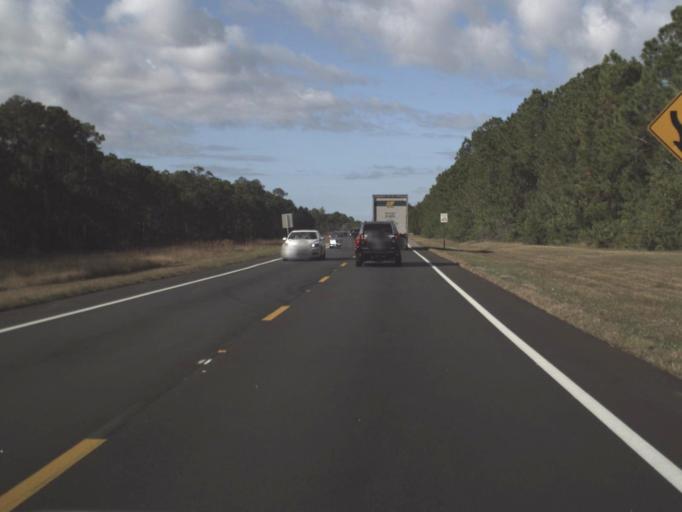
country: US
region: Florida
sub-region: Volusia County
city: South Daytona
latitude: 29.1521
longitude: -81.0634
